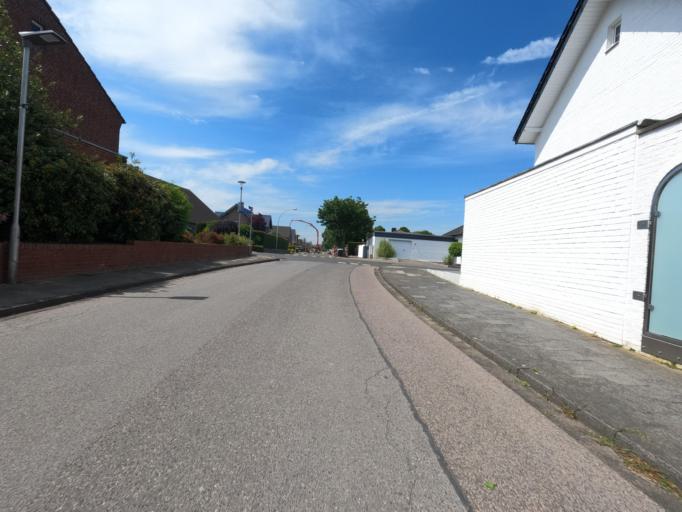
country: DE
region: North Rhine-Westphalia
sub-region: Regierungsbezirk Koln
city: Ubach-Palenberg
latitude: 50.9160
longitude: 6.1106
